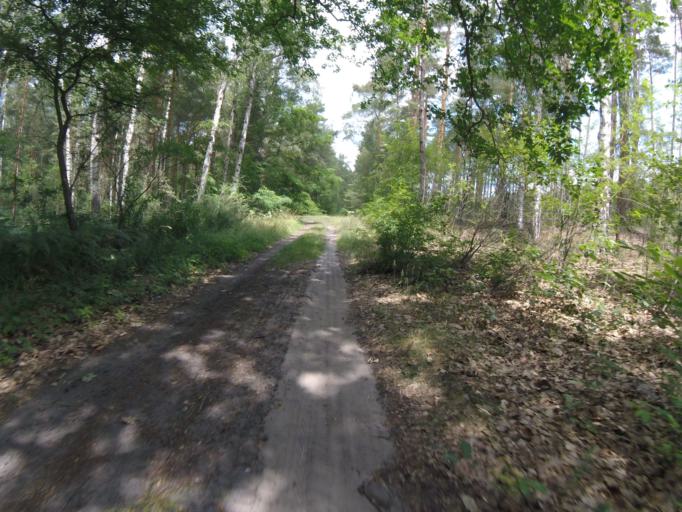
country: DE
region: Brandenburg
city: Gross Koris
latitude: 52.1978
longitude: 13.6477
